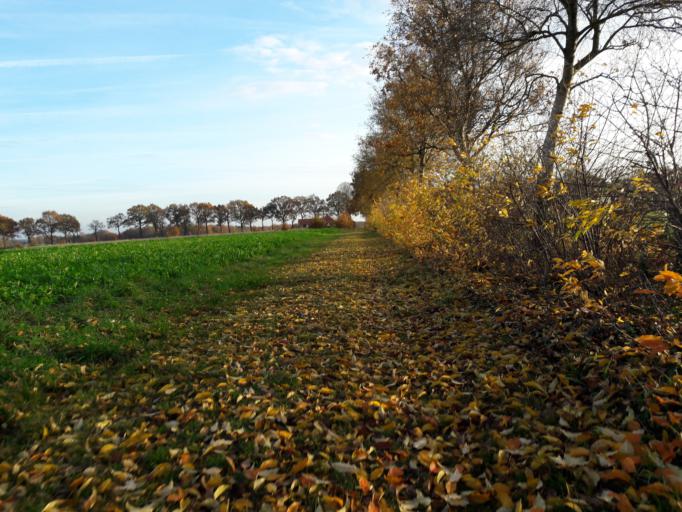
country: NL
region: Drenthe
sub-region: Gemeente Borger-Odoorn
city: Borger
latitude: 52.9583
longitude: 6.8141
